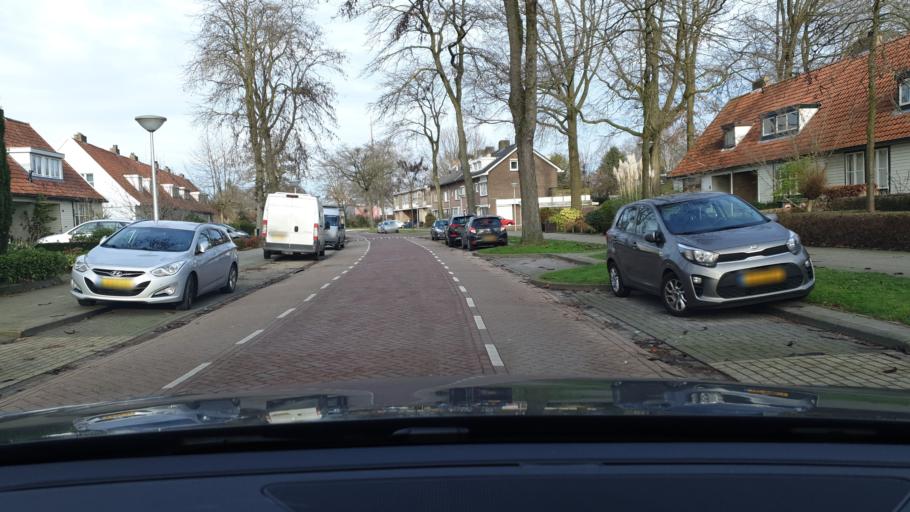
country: NL
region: North Brabant
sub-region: Gemeente Eindhoven
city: De Doornakkers
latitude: 51.4411
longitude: 5.5145
